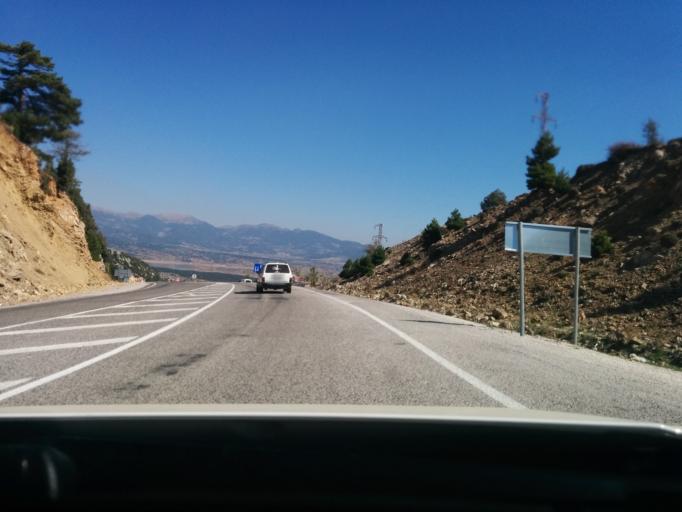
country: TR
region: Mugla
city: Seki
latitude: 36.7891
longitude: 29.4967
